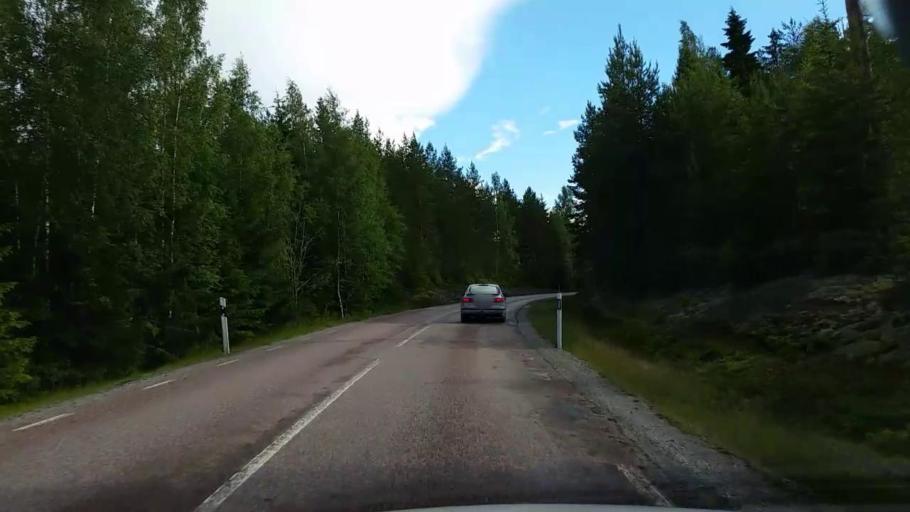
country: SE
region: Vaestmanland
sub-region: Fagersta Kommun
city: Fagersta
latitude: 59.9220
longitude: 15.8315
